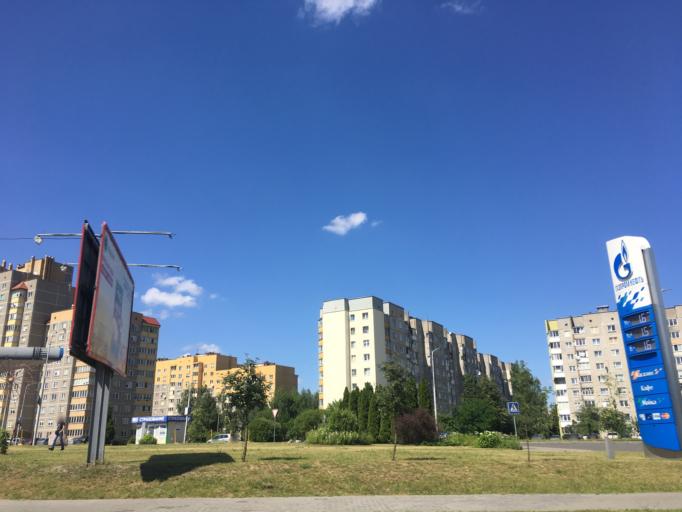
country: BY
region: Grodnenskaya
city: Hrodna
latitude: 53.6482
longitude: 23.8370
